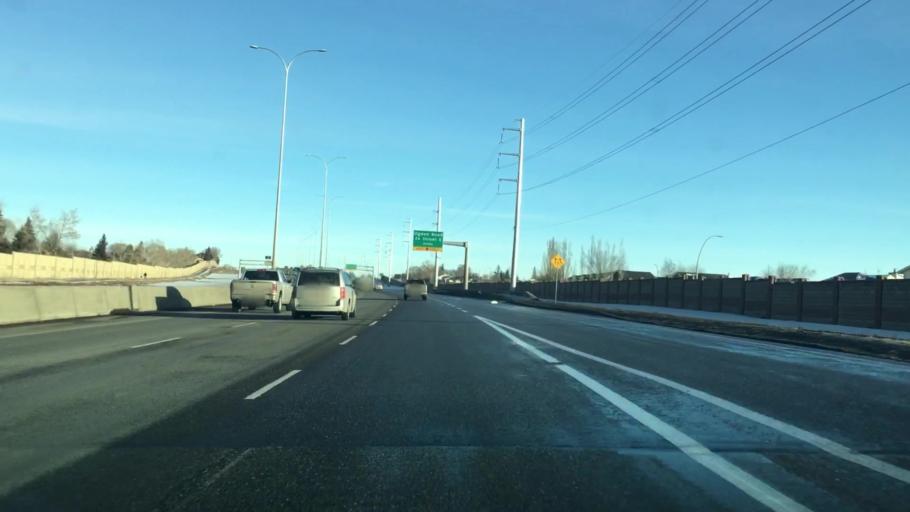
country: CA
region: Alberta
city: Calgary
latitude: 50.9794
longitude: -114.0101
